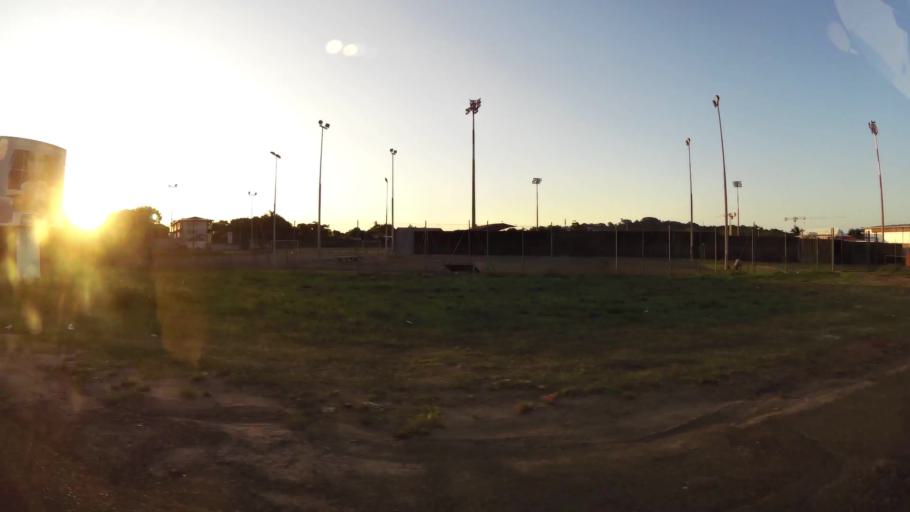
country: GF
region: Guyane
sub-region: Guyane
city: Cayenne
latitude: 4.9320
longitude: -52.3118
